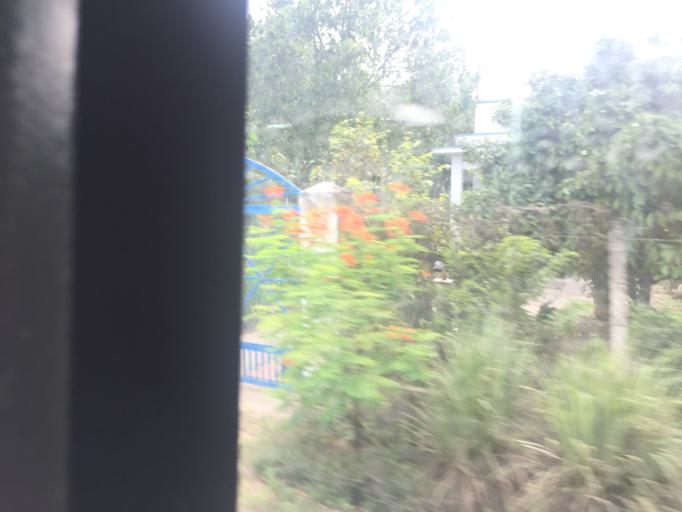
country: VN
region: Tay Ninh
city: Trang Bang
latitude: 11.1386
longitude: 106.4738
